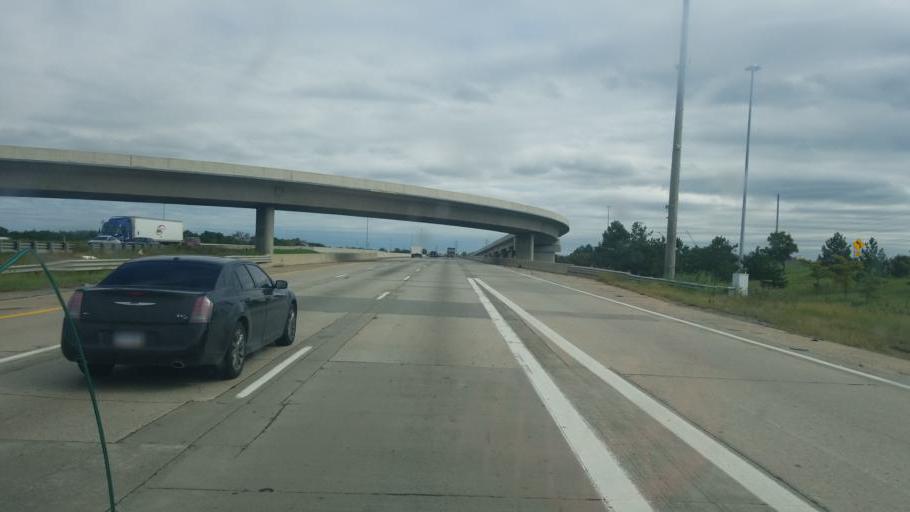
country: US
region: Michigan
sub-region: Wayne County
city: Allen Park
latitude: 42.2667
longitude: -83.2265
